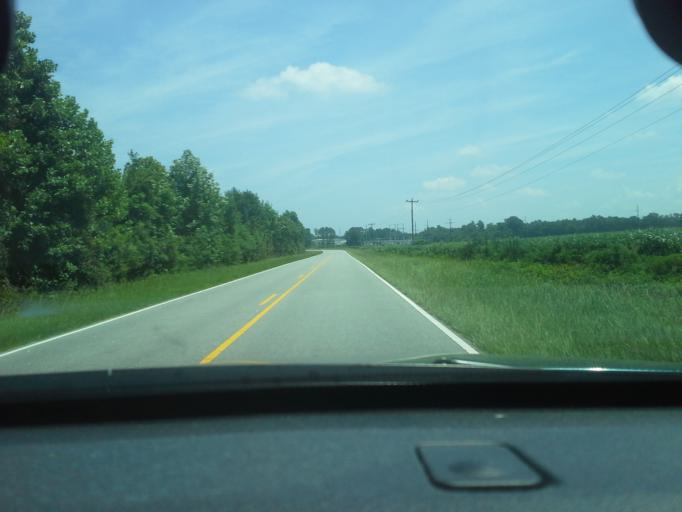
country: US
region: North Carolina
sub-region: Chowan County
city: Edenton
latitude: 35.9251
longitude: -76.6271
